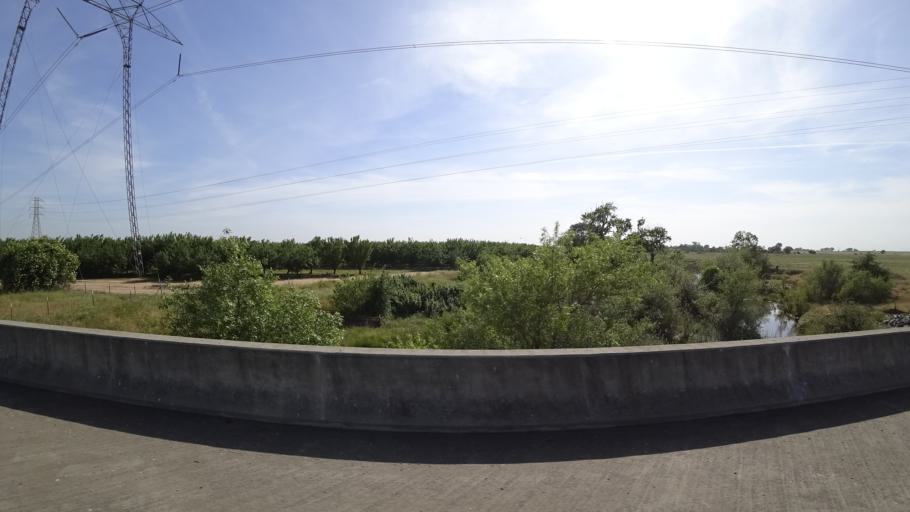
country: US
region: California
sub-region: Butte County
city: Thermalito
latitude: 39.6078
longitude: -121.6727
